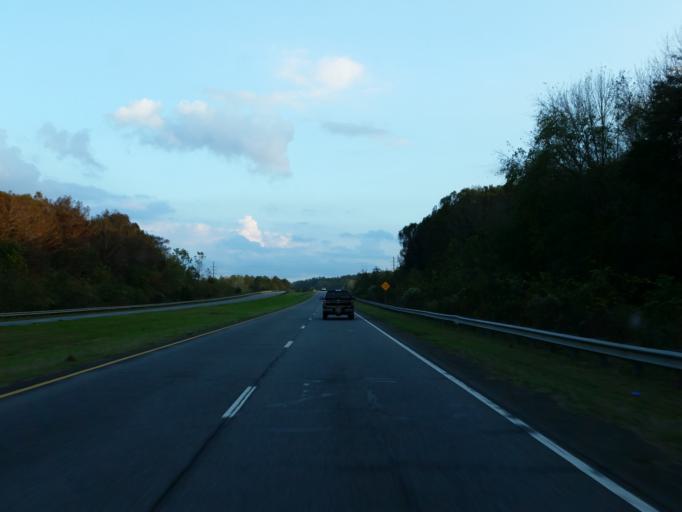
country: US
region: Georgia
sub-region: Houston County
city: Perry
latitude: 32.4070
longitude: -83.6469
